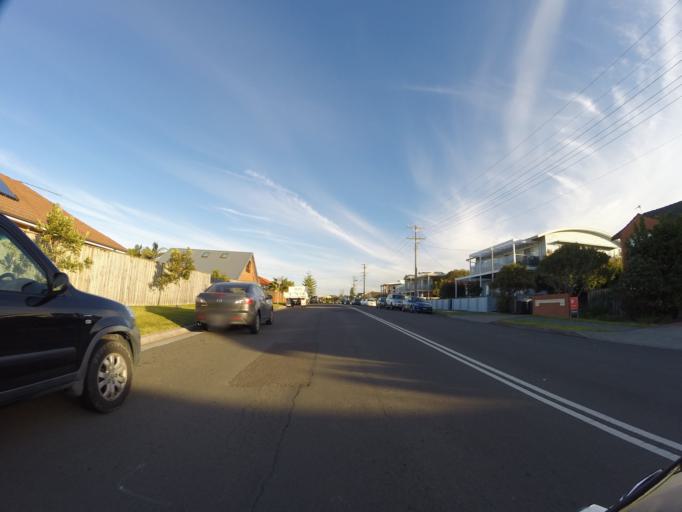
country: AU
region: New South Wales
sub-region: Wollongong
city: Bulli
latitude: -34.3476
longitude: 150.9182
